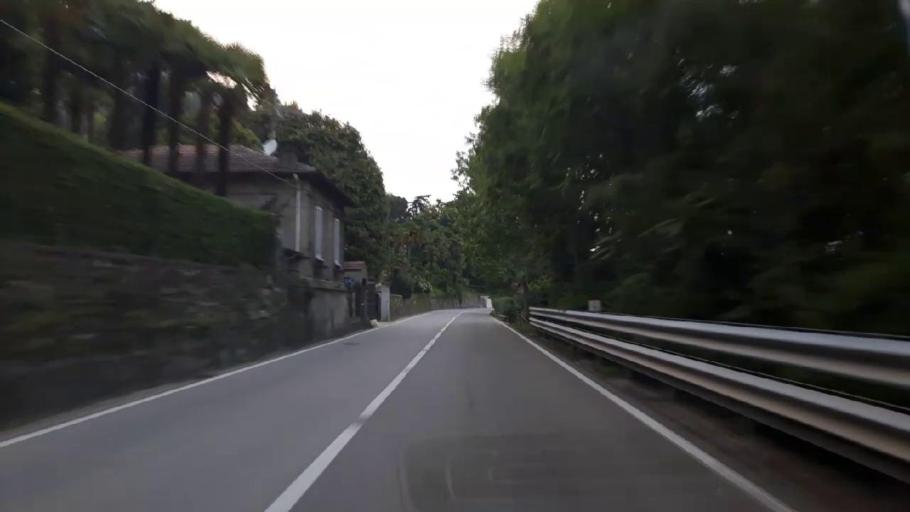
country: IT
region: Piedmont
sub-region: Provincia Verbano-Cusio-Ossola
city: Belgirate
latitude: 45.8557
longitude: 8.5688
